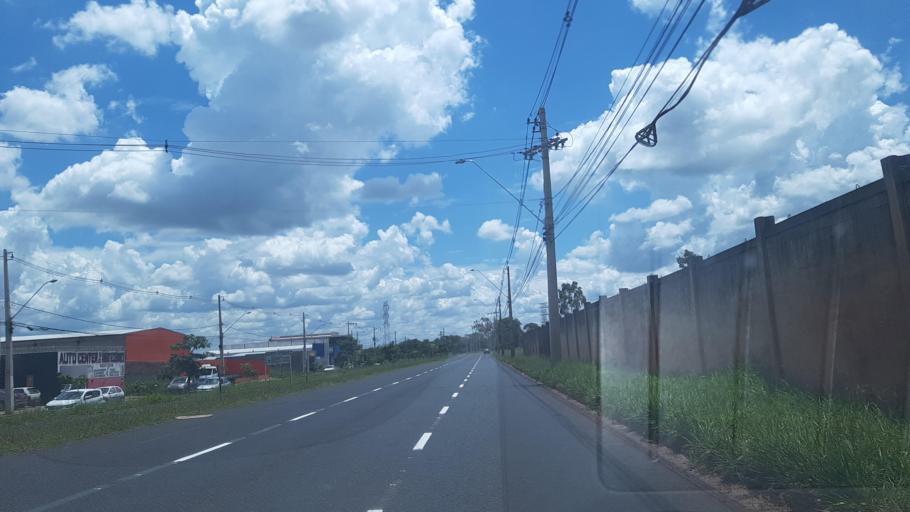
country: BR
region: Minas Gerais
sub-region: Uberlandia
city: Uberlandia
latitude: -18.9632
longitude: -48.3412
